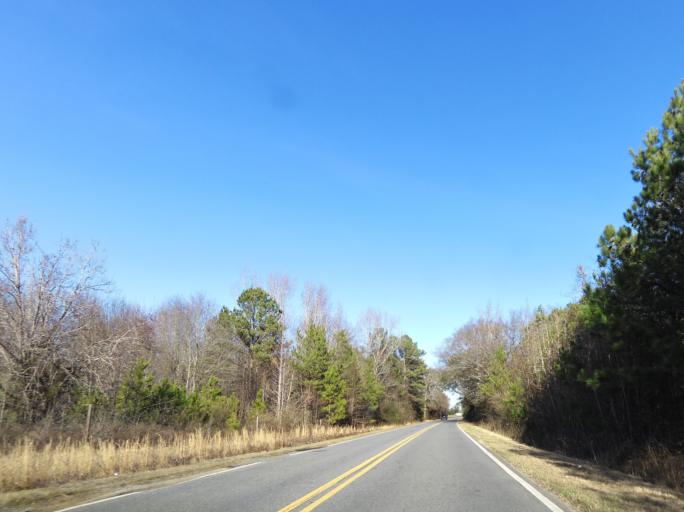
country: US
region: Georgia
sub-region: Bibb County
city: West Point
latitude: 32.7713
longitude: -83.8325
